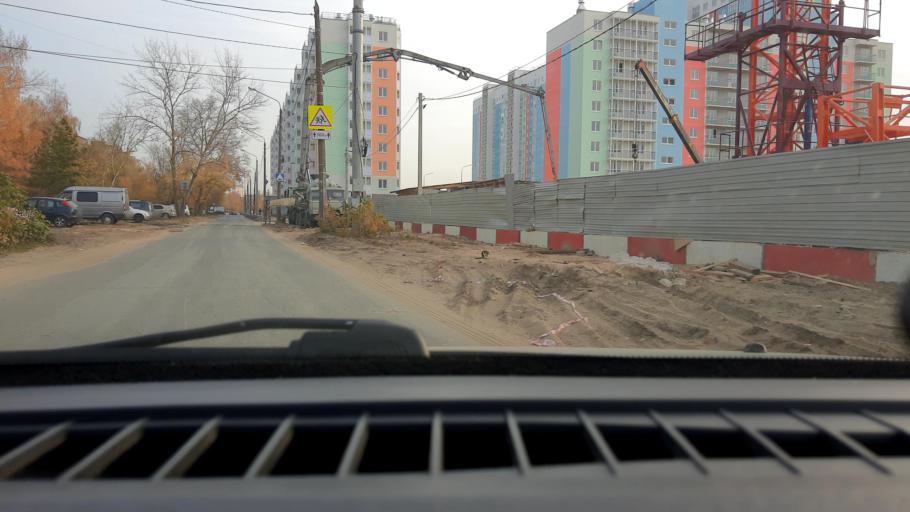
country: RU
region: Nizjnij Novgorod
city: Gorbatovka
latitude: 56.3642
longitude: 43.8015
